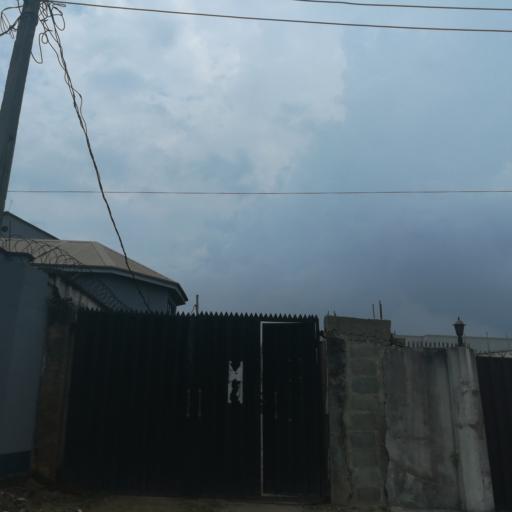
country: NG
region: Lagos
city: Ojota
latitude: 6.5737
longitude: 3.3837
